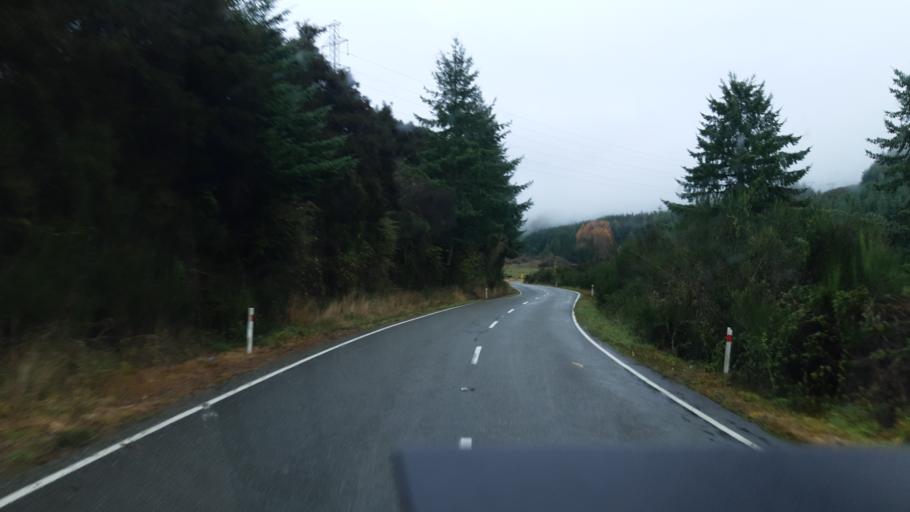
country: NZ
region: Tasman
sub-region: Tasman District
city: Wakefield
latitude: -41.6714
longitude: 172.8756
